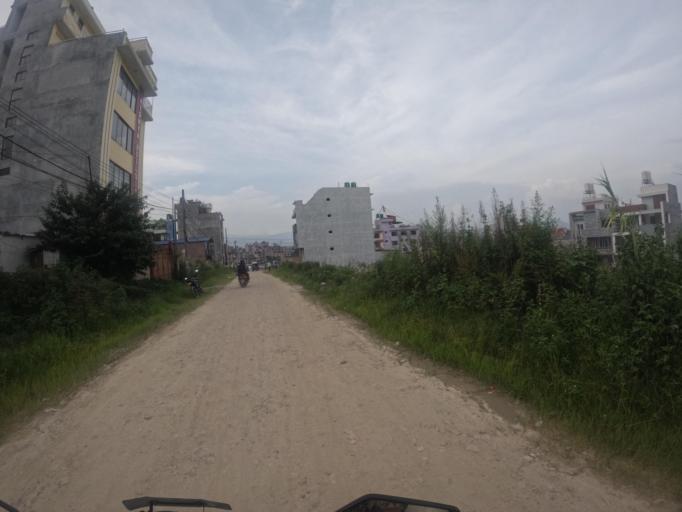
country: NP
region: Central Region
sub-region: Bagmati Zone
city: Bhaktapur
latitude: 27.6802
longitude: 85.3938
